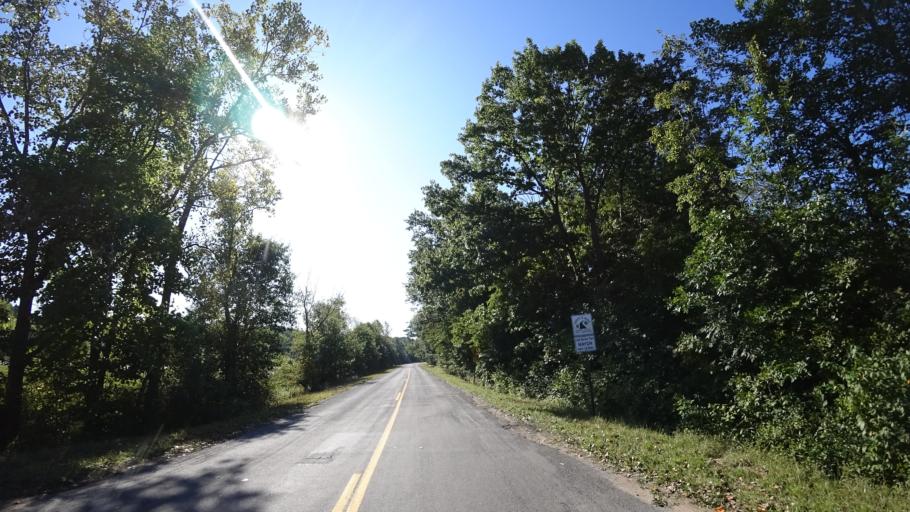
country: US
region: Michigan
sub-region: Berrien County
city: Stevensville
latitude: 42.0106
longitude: -86.5351
